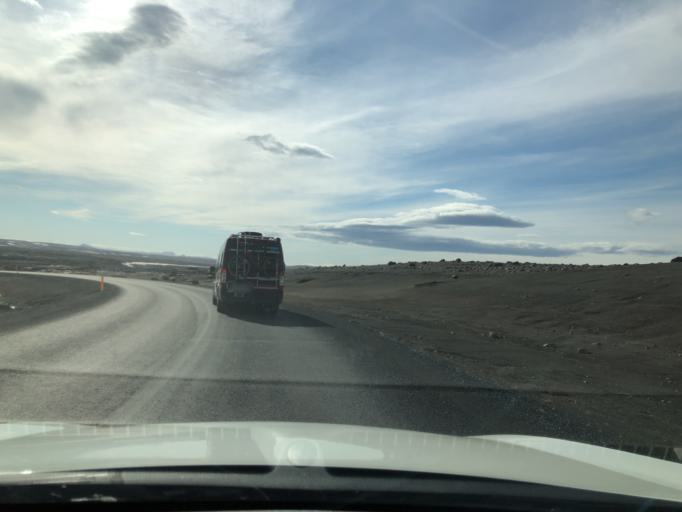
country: IS
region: Northeast
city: Husavik
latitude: 65.8110
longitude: -16.4054
